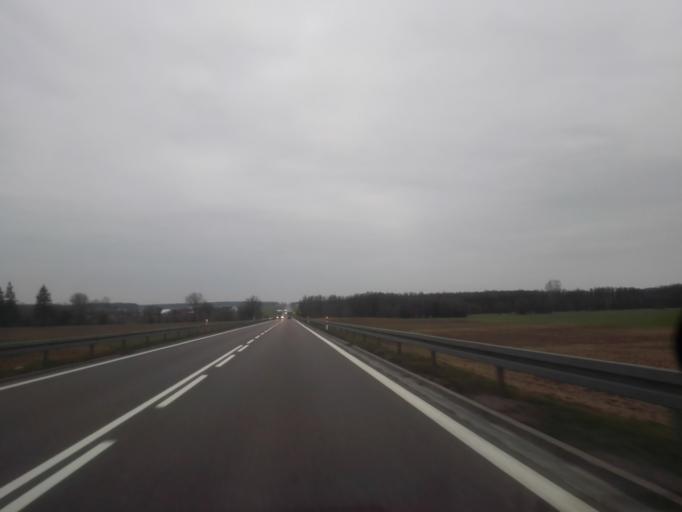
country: PL
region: Podlasie
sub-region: Powiat grajewski
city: Szczuczyn
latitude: 53.5066
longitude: 22.2381
